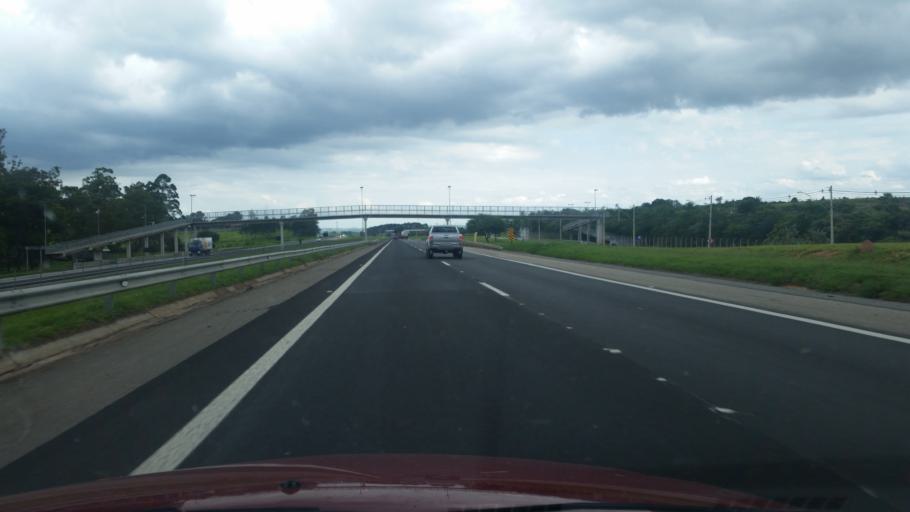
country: BR
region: Sao Paulo
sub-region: Sorocaba
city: Sorocaba
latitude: -23.3686
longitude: -47.4618
